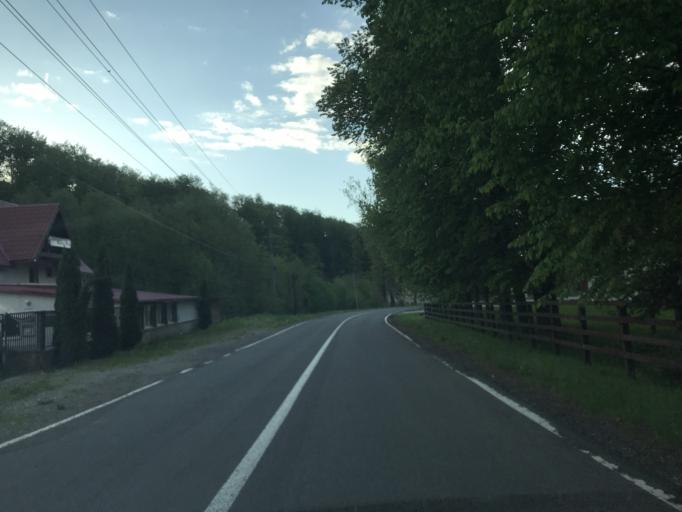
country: RO
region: Sibiu
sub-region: Comuna Cartisoara
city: Cartisoara
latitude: 45.6828
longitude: 24.5760
